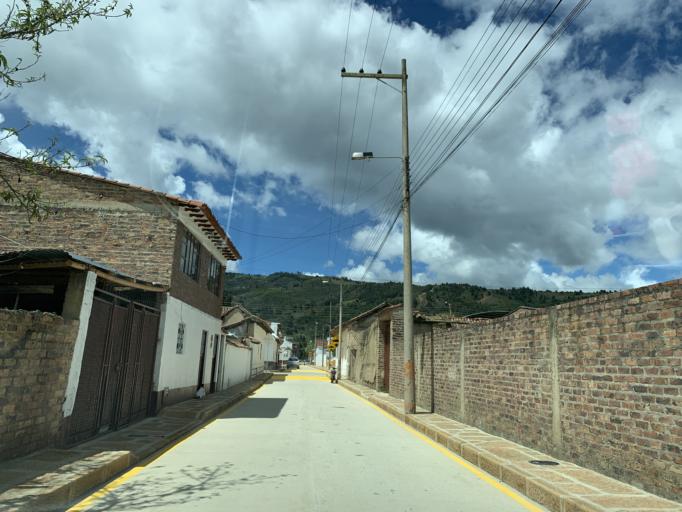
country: CO
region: Boyaca
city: Floresta
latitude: 5.8585
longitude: -72.9190
